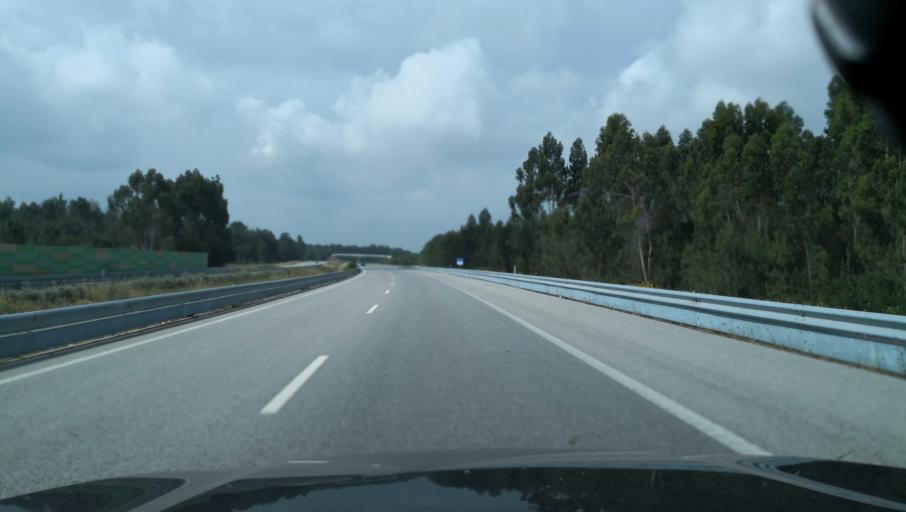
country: PT
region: Coimbra
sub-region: Montemor-O-Velho
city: Arazede
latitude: 40.2982
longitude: -8.7404
